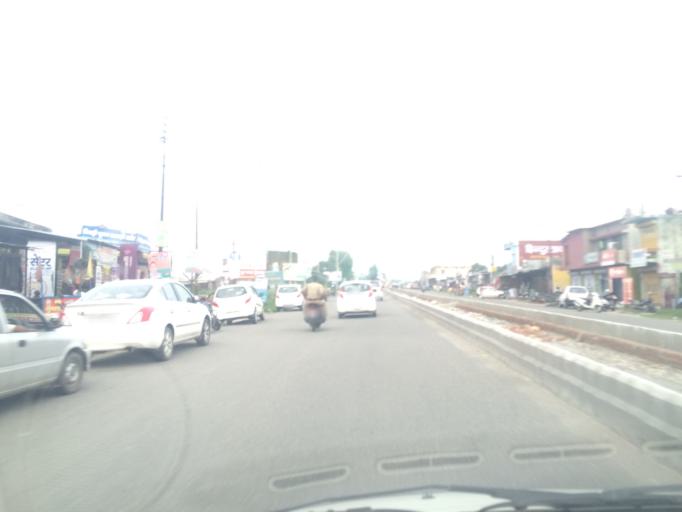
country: IN
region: Uttarakhand
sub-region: Dehradun
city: Doiwala
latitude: 30.1876
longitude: 78.1552
